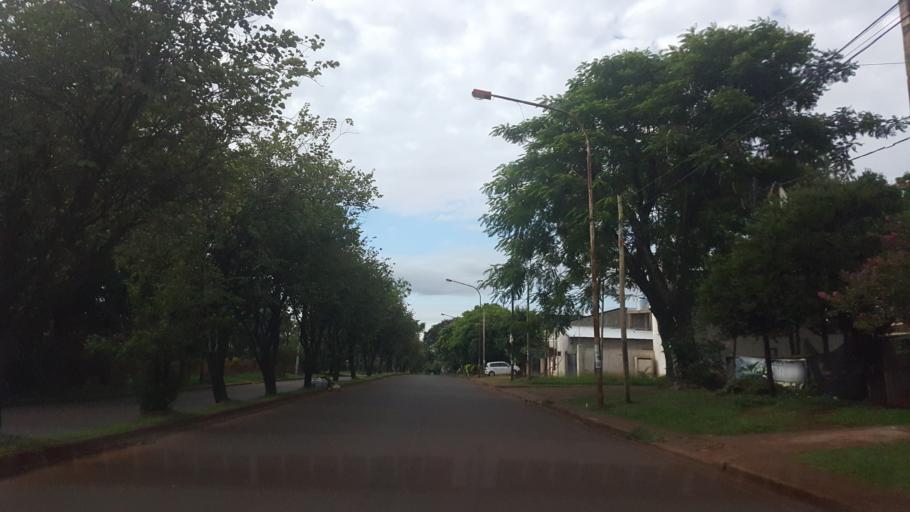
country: AR
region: Misiones
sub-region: Departamento de Capital
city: Posadas
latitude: -27.4001
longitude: -55.9363
